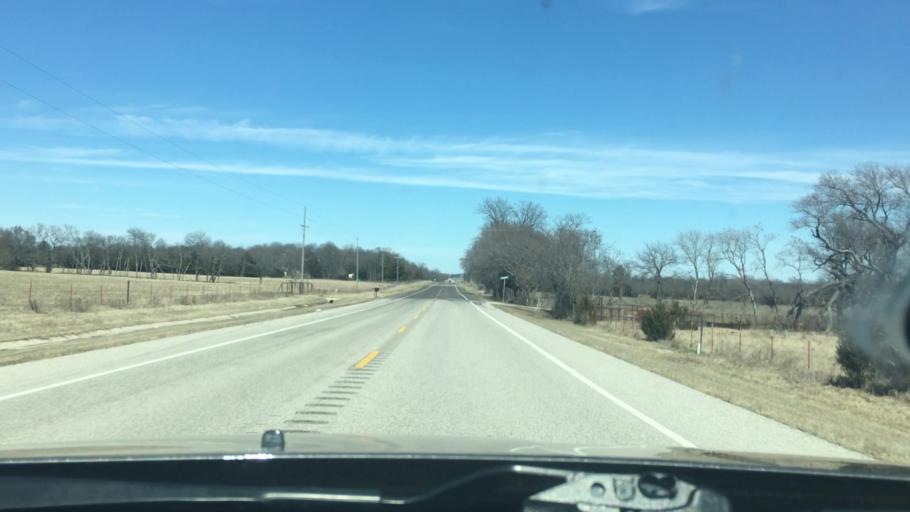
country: US
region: Oklahoma
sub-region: Murray County
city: Sulphur
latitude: 34.3515
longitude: -96.9509
